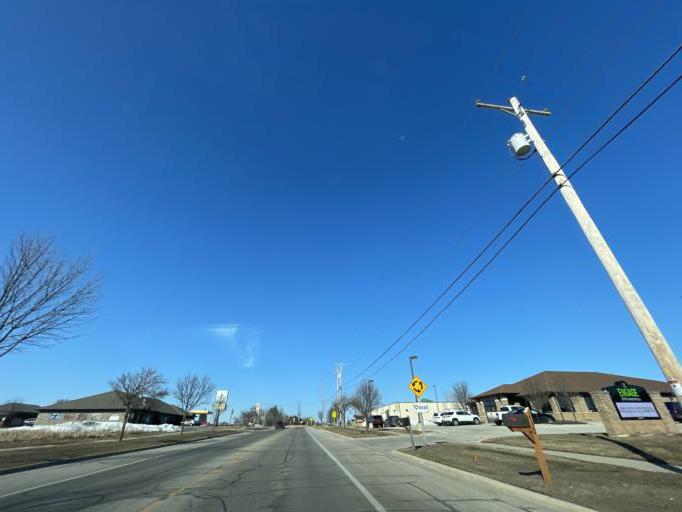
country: US
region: Wisconsin
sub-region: Brown County
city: Howard
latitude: 44.5894
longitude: -88.0843
